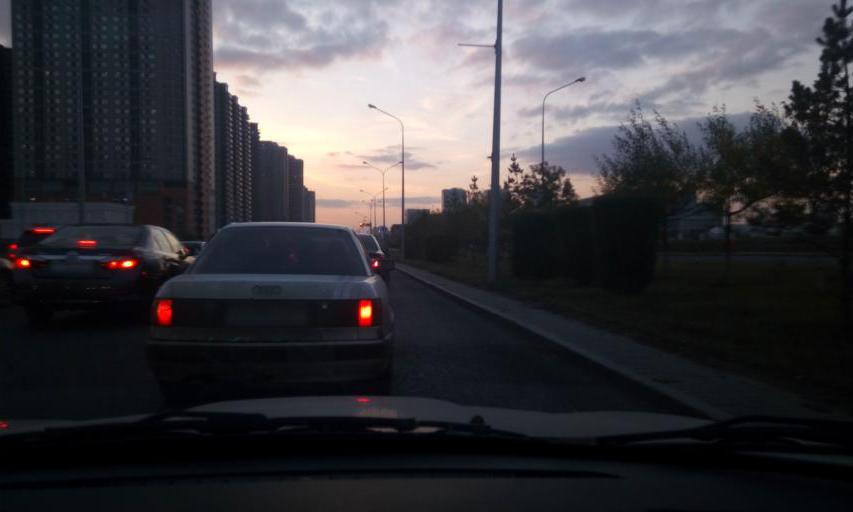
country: KZ
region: Astana Qalasy
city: Astana
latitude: 51.1272
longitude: 71.4735
